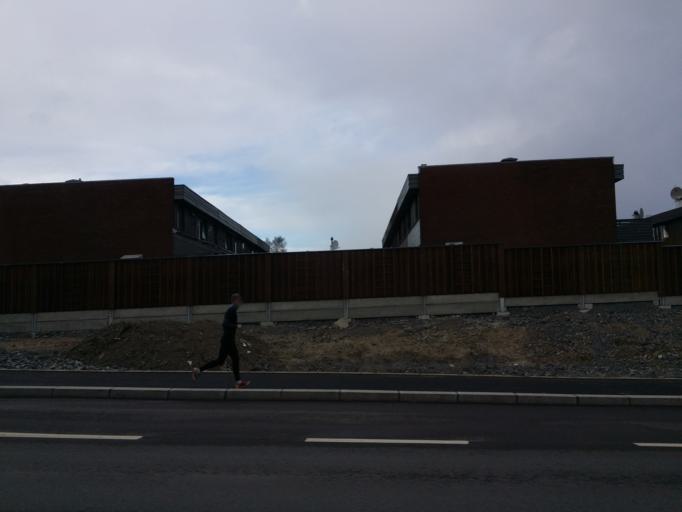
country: NO
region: Oslo
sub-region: Oslo
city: Oslo
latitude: 59.9337
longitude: 10.7948
